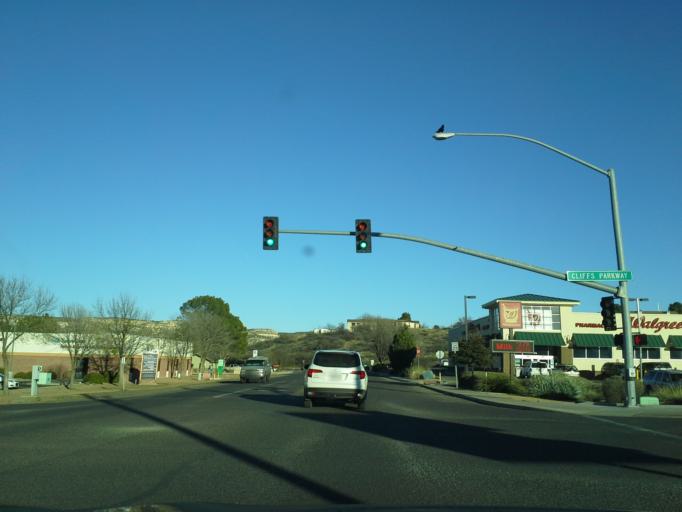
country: US
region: Arizona
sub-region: Yavapai County
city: Camp Verde
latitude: 34.5657
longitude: -111.8632
